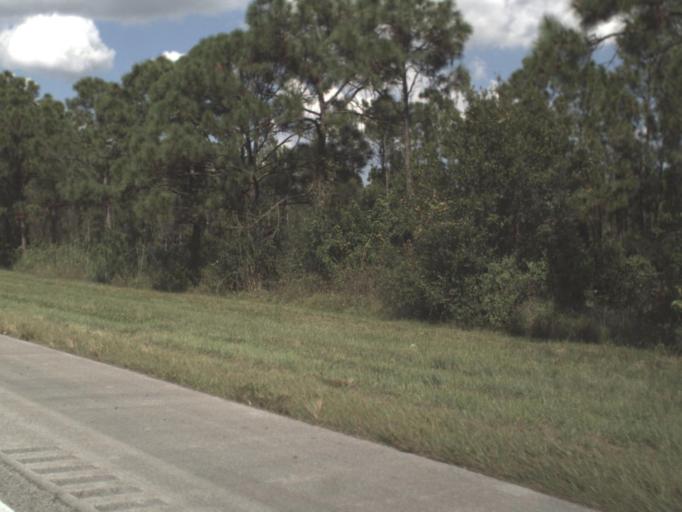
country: US
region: Florida
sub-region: Saint Lucie County
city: Fort Pierce South
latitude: 27.4282
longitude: -80.4143
